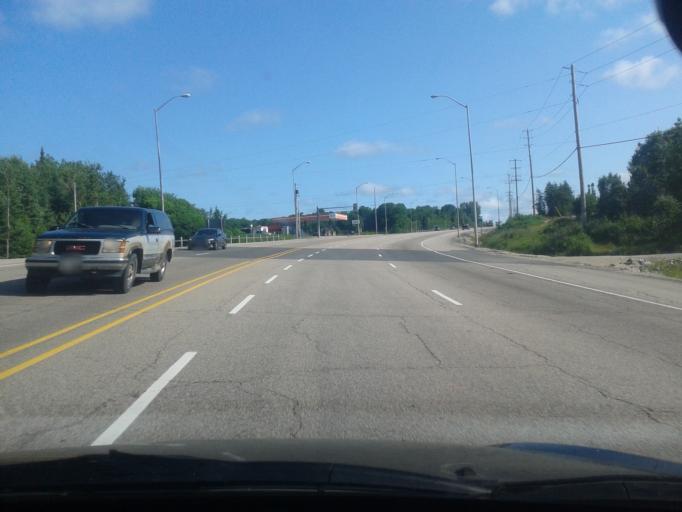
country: CA
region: Ontario
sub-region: Nipissing District
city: North Bay
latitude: 46.3449
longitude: -79.4714
